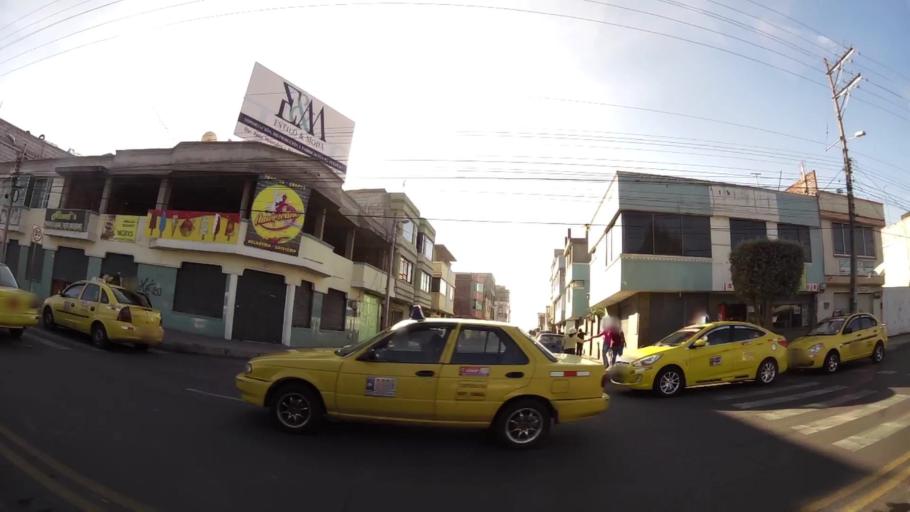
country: EC
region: Chimborazo
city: Riobamba
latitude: -1.6577
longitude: -78.6457
